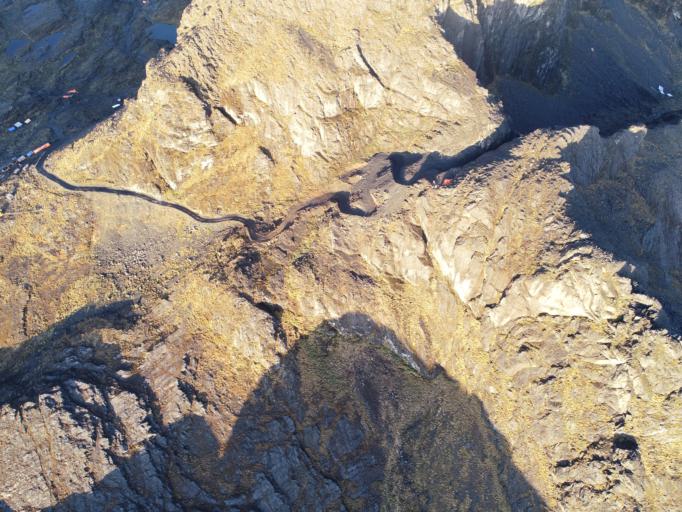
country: PE
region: Puno
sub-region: San Antonio De Putina
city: Sina
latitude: -14.7366
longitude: -69.0479
